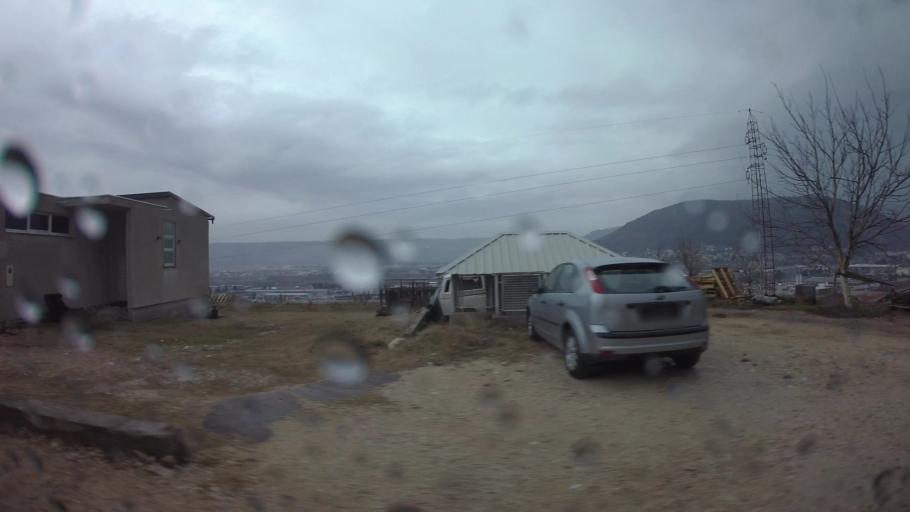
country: BA
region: Federation of Bosnia and Herzegovina
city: Rodoc
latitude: 43.3128
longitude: 17.8378
